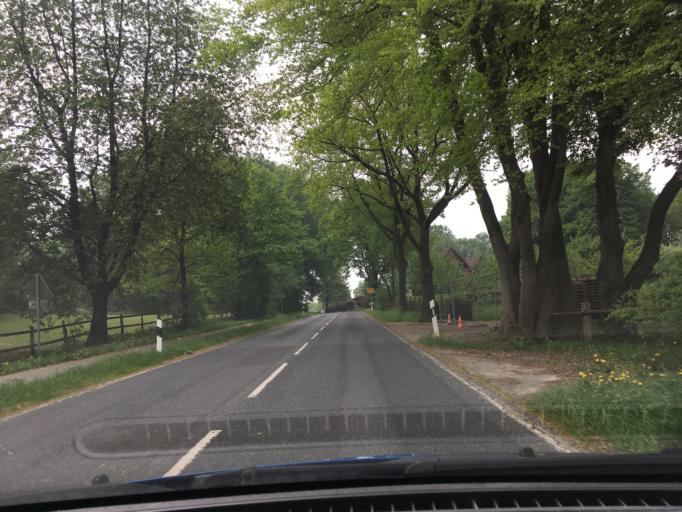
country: DE
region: Lower Saxony
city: Buchholz in der Nordheide
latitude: 53.3997
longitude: 9.8617
